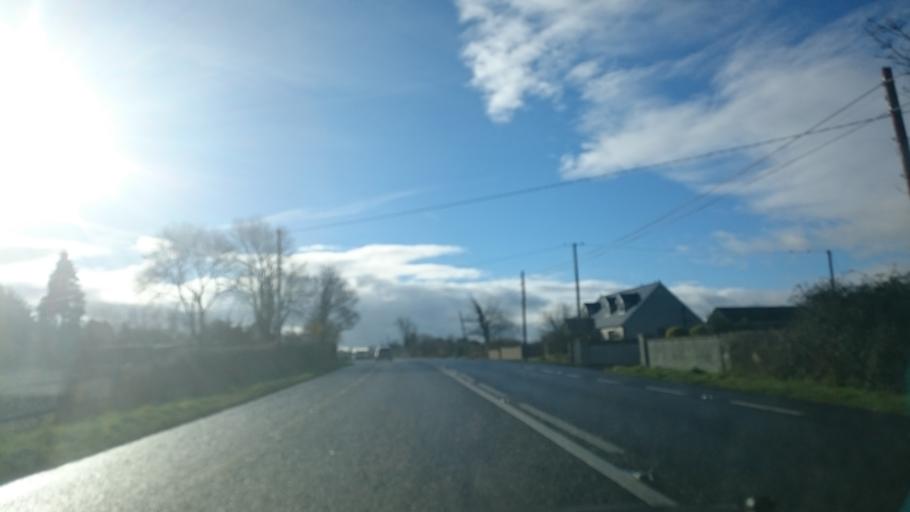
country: IE
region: Leinster
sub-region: Kilkenny
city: Kilkenny
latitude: 52.5979
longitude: -7.3050
